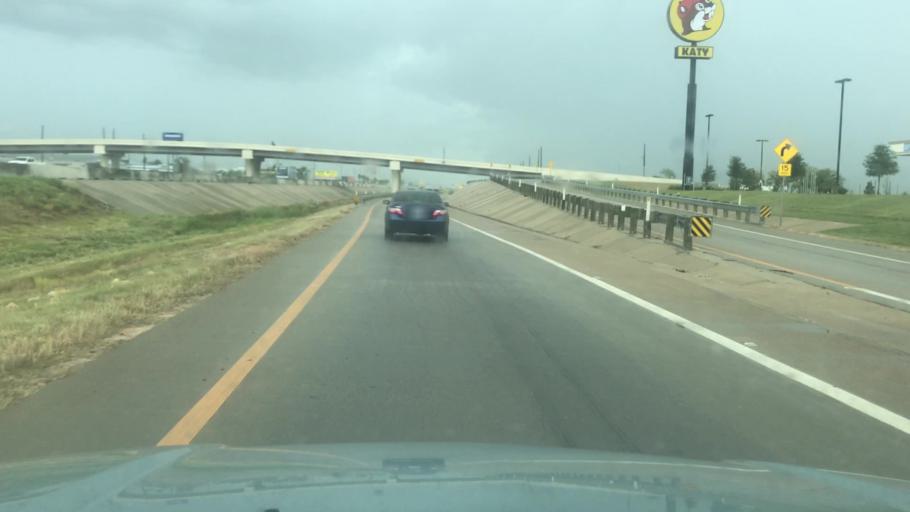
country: US
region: Texas
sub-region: Harris County
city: Katy
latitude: 29.7776
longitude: -95.8481
